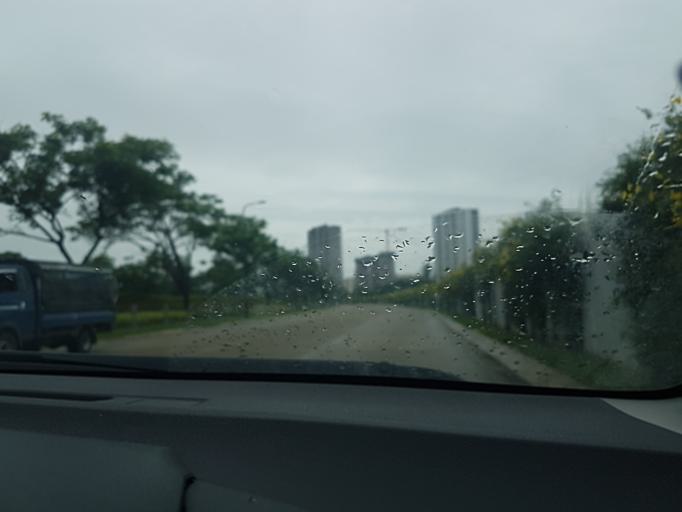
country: MM
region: Yangon
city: Syriam
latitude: 16.7769
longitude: 96.2336
